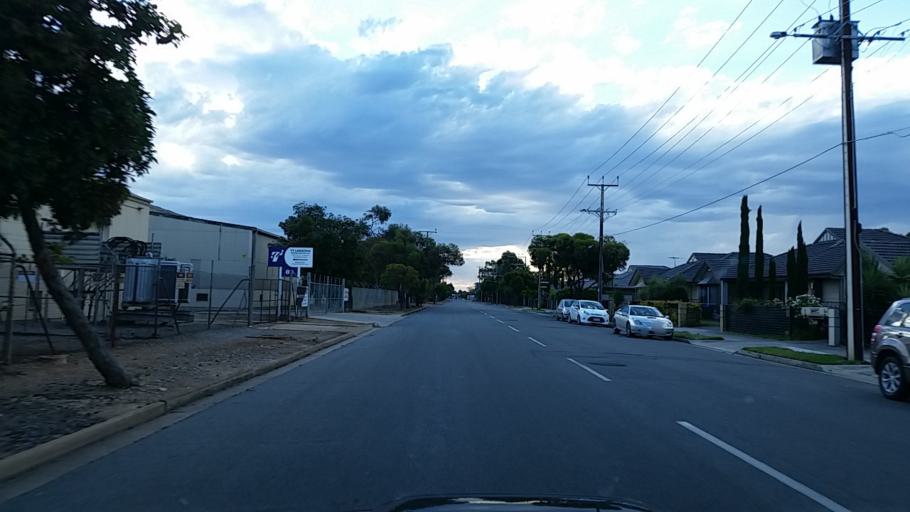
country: AU
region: South Australia
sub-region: Charles Sturt
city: Woodville North
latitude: -34.8627
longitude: 138.5424
